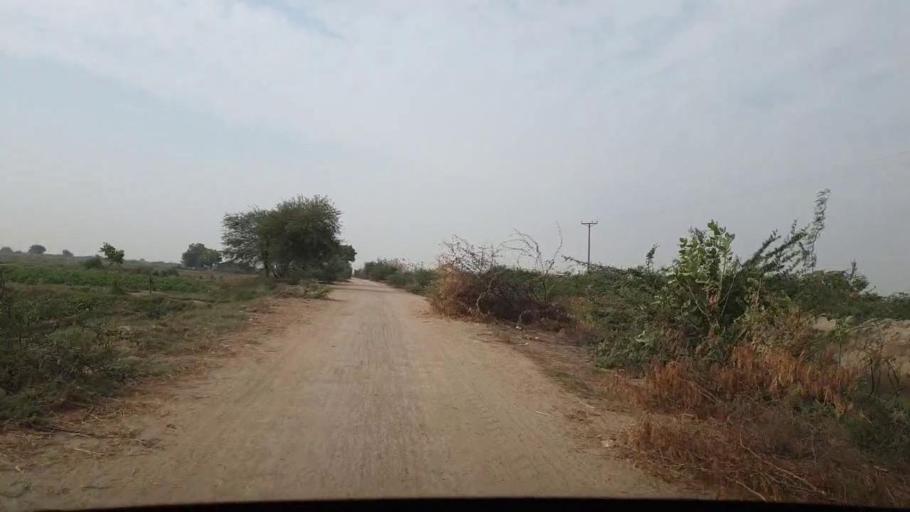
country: PK
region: Sindh
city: Chuhar Jamali
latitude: 24.4109
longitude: 67.9190
